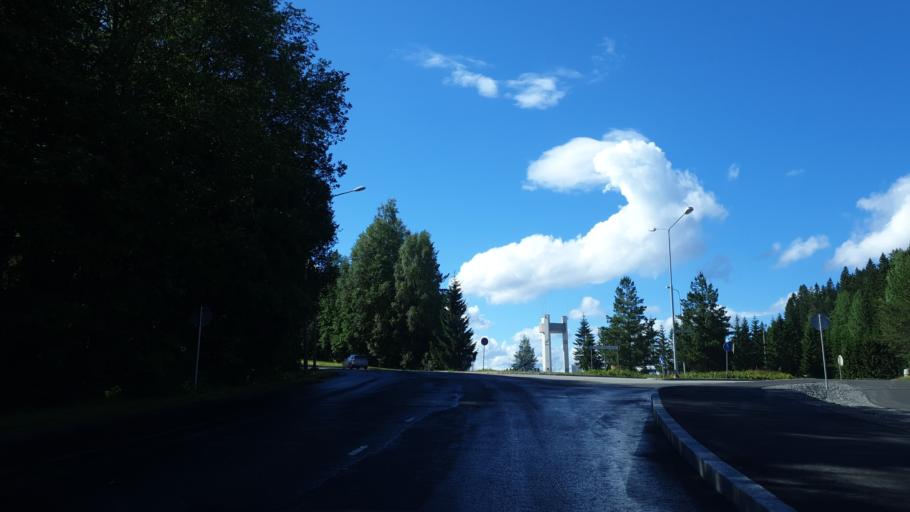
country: FI
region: Northern Savo
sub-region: Kuopio
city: Kuopio
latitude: 62.9055
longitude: 27.6528
